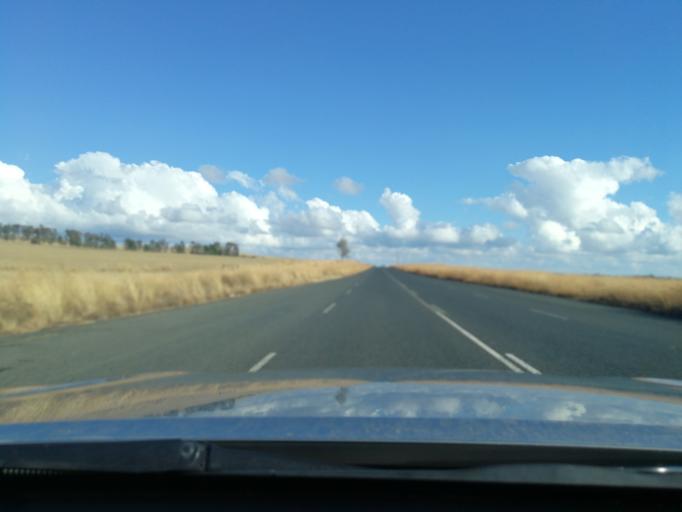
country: ZA
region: Orange Free State
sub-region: Thabo Mofutsanyana District Municipality
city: Bethlehem
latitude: -28.0410
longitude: 28.3689
